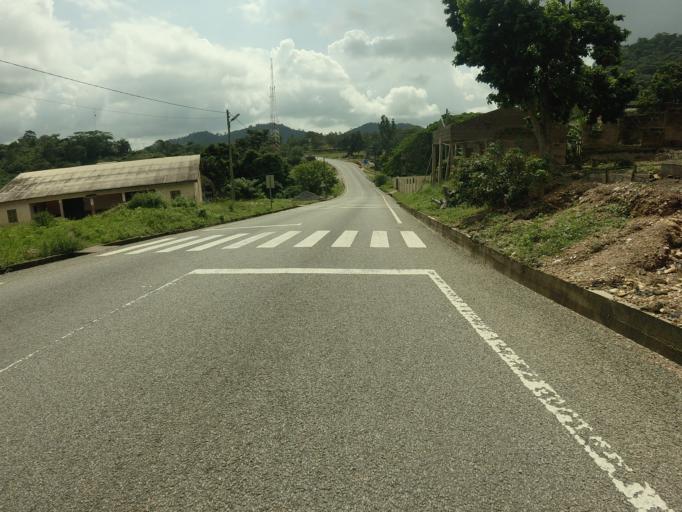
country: GH
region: Volta
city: Kpandu
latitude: 6.8233
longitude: 0.4226
